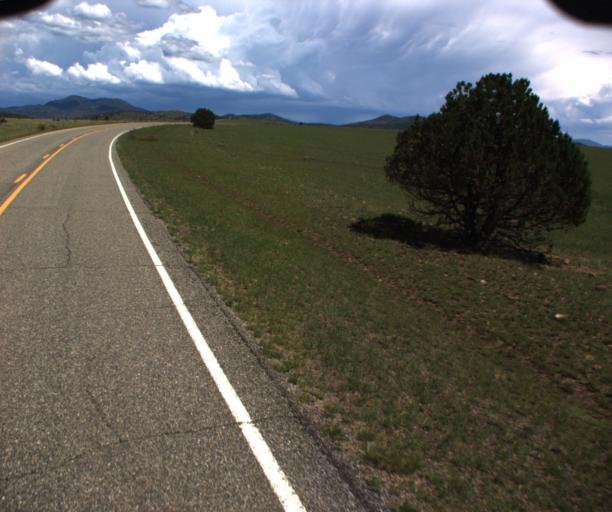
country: US
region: Arizona
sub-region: Greenlee County
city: Morenci
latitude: 33.3115
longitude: -109.3508
